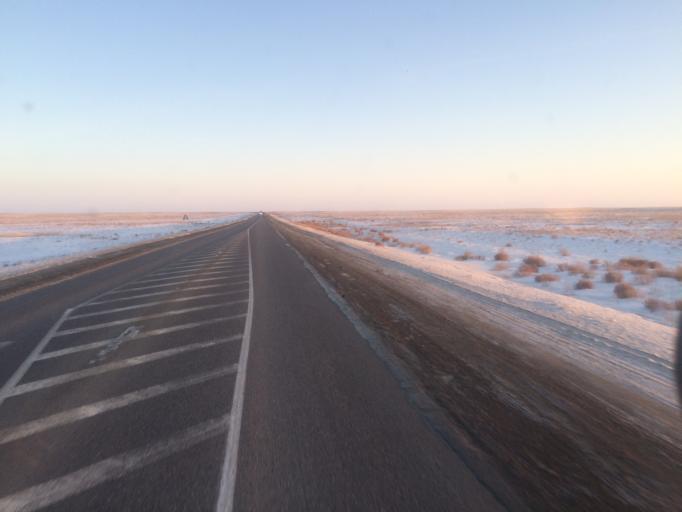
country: KZ
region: Qyzylorda
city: Sekseuil
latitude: 47.6801
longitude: 61.4417
